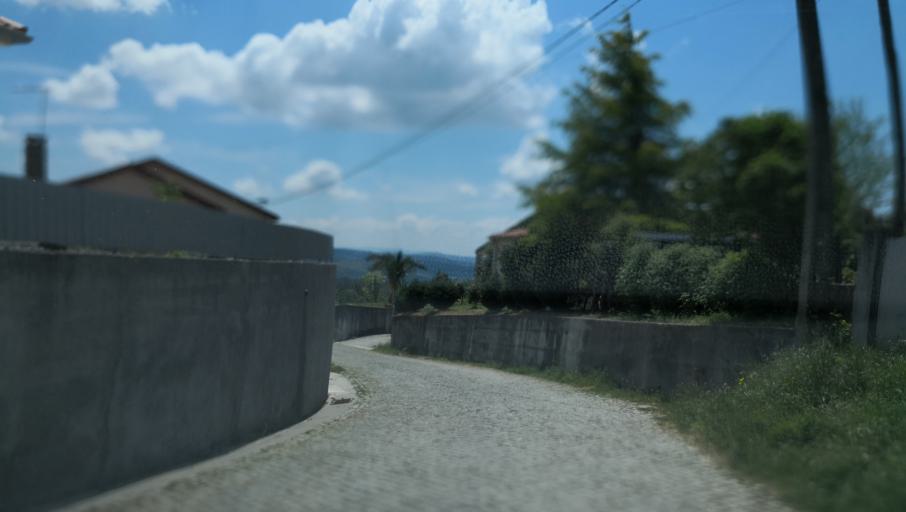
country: PT
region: Vila Real
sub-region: Vila Real
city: Vila Real
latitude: 41.3598
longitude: -7.7294
